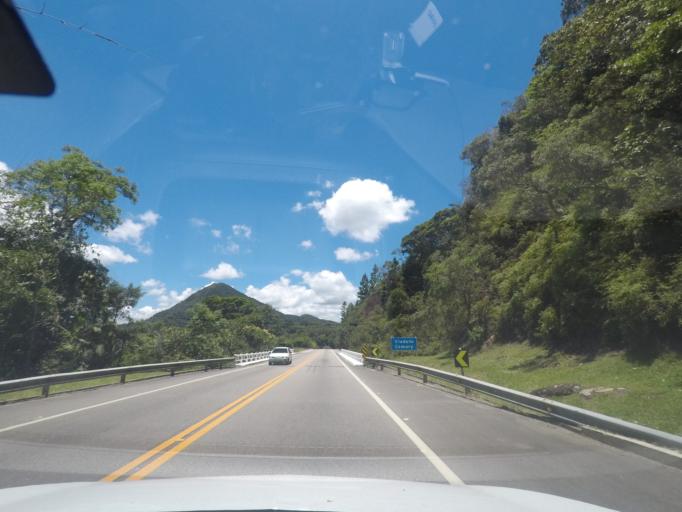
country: BR
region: Rio de Janeiro
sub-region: Teresopolis
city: Teresopolis
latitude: -22.4595
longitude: -42.9786
